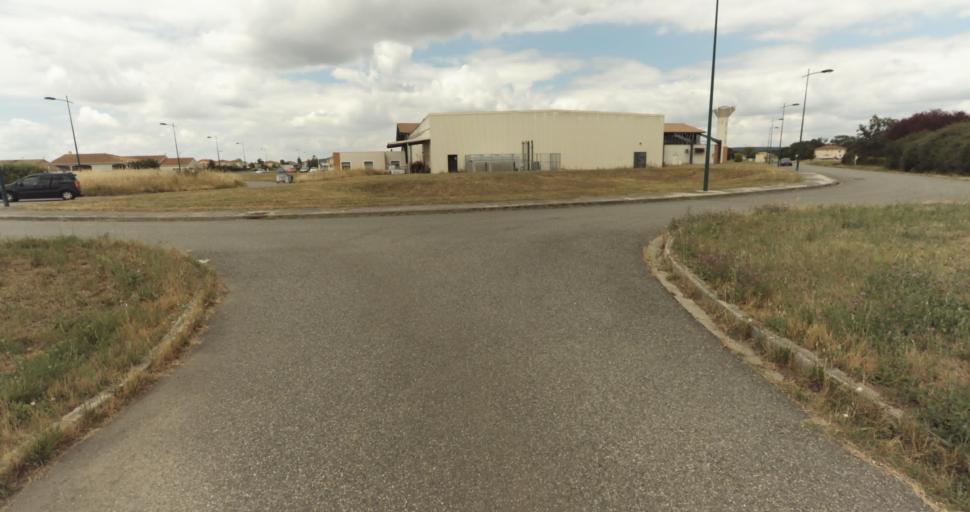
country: FR
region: Midi-Pyrenees
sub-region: Departement de la Haute-Garonne
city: Fontenilles
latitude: 43.5470
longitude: 1.1944
